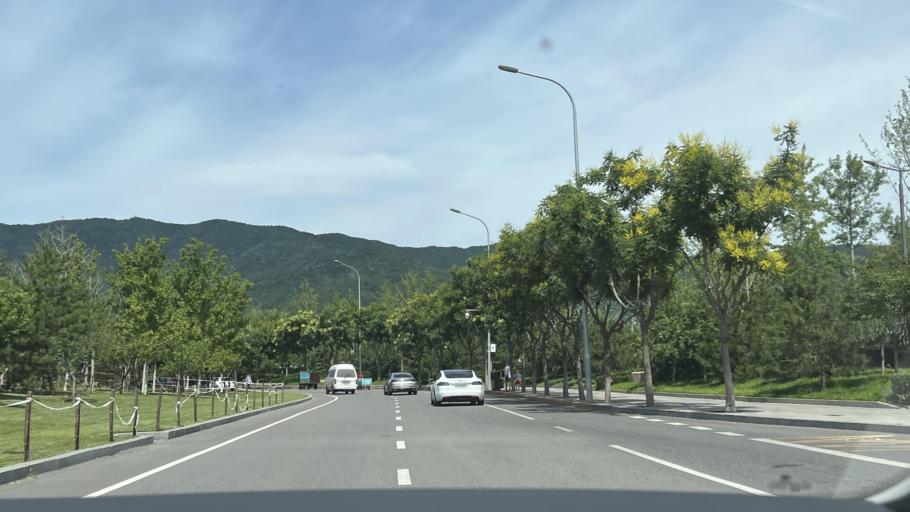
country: CN
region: Beijing
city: Xiangshan
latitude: 39.9922
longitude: 116.2143
